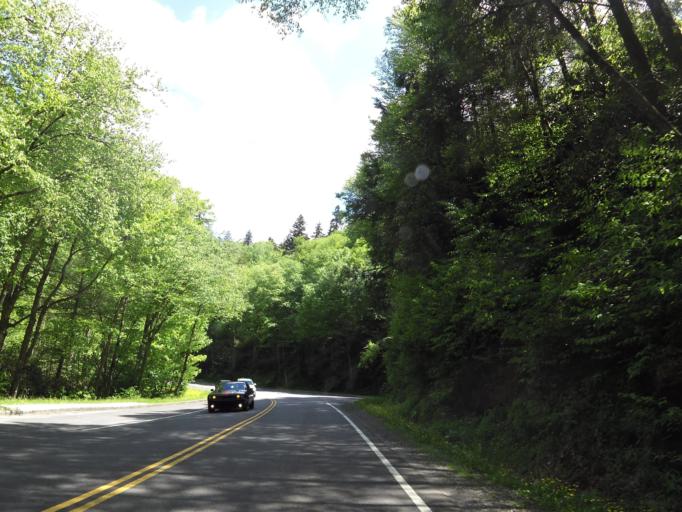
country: US
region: Tennessee
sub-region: Sevier County
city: Gatlinburg
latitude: 35.6219
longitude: -83.4390
